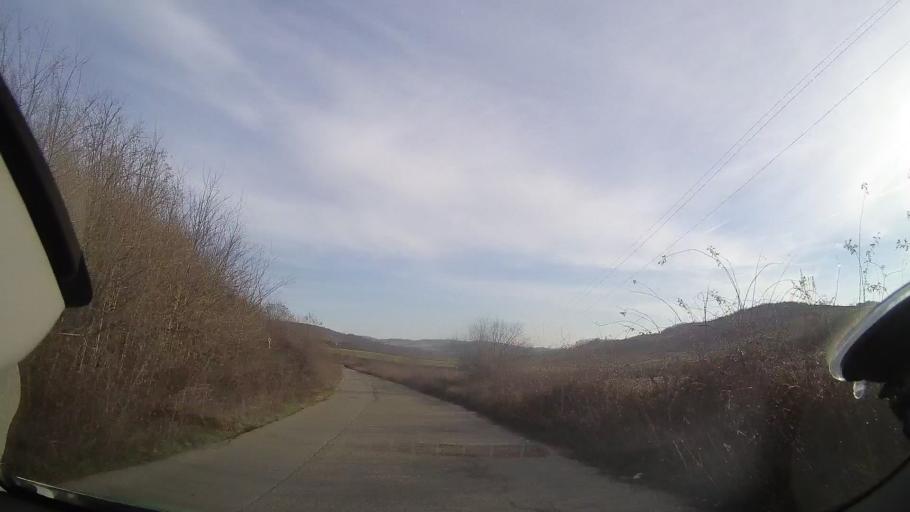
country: RO
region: Bihor
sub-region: Comuna Sarbi
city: Sarbi
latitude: 47.1800
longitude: 22.1371
